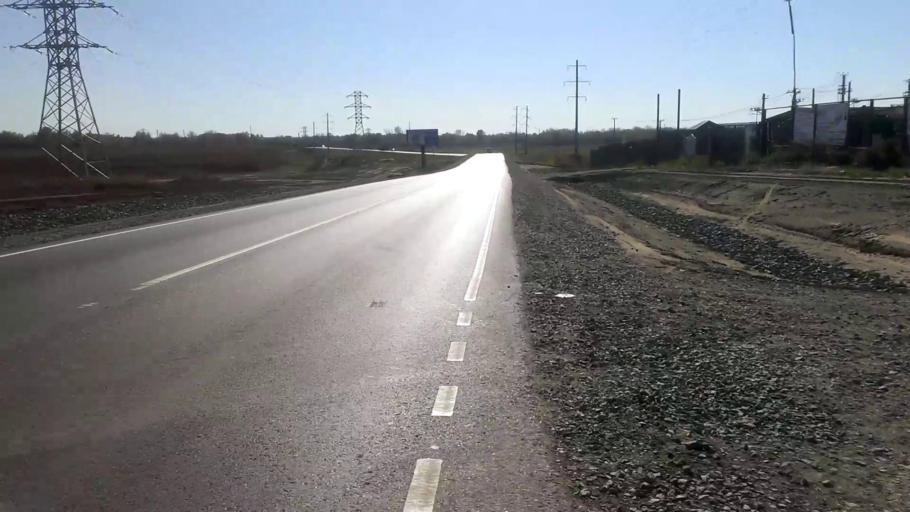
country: RU
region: Altai Krai
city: Sannikovo
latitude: 53.3357
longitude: 83.9385
